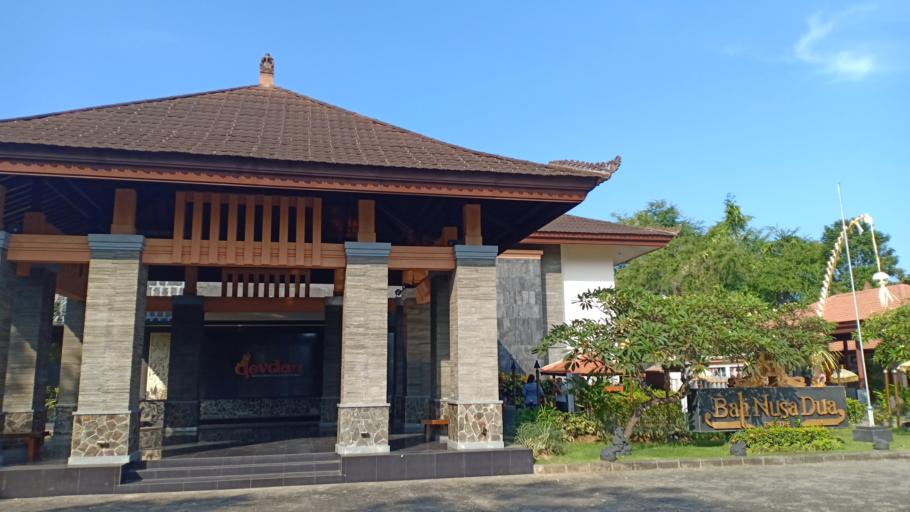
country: ID
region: Bali
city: Bualu
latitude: -8.8006
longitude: 115.2336
